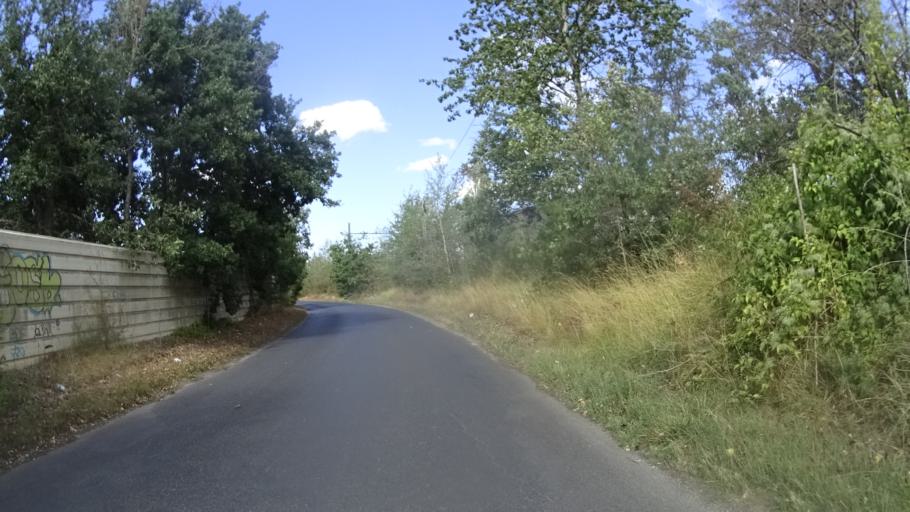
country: FR
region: Ile-de-France
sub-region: Departement de l'Essonne
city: Maisse
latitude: 48.3857
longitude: 2.3900
